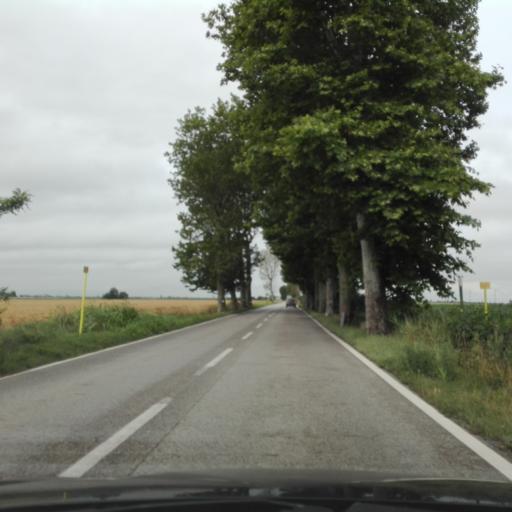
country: IT
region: Veneto
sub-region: Provincia di Padova
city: Barbona
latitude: 45.0781
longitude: 11.7157
